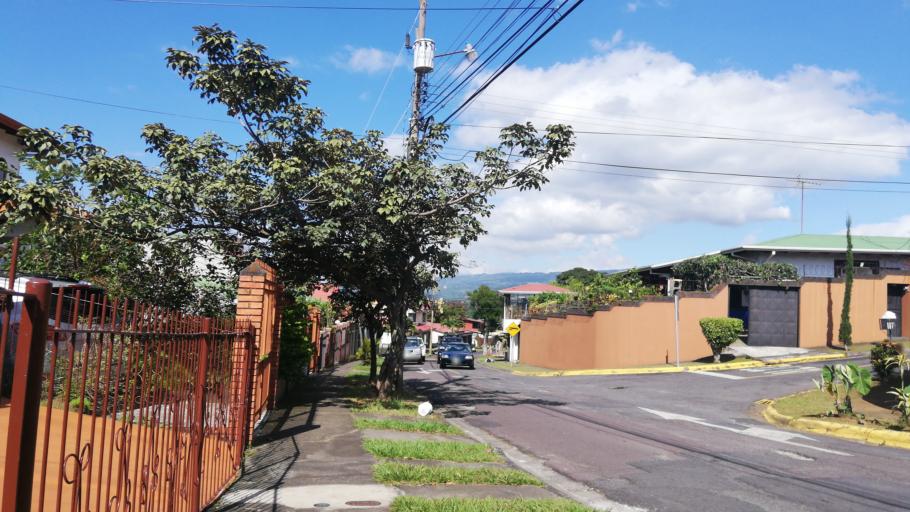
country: CR
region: Alajuela
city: San Juan
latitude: 10.0782
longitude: -84.3080
